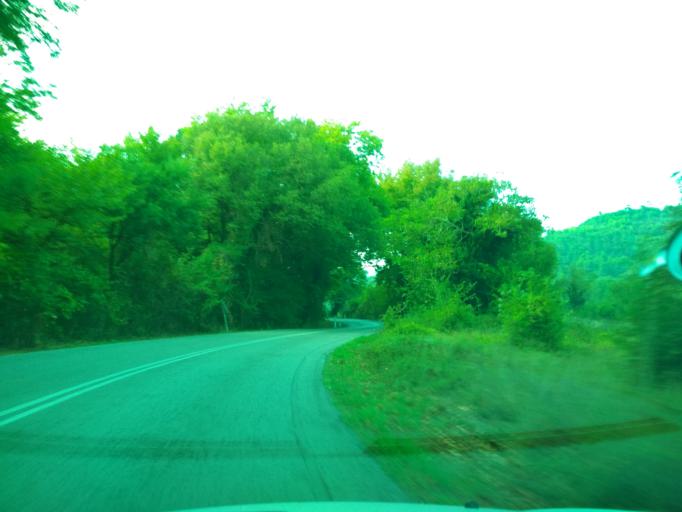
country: GR
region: Central Greece
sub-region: Nomos Evvoias
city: Prokopion
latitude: 38.7620
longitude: 23.4788
